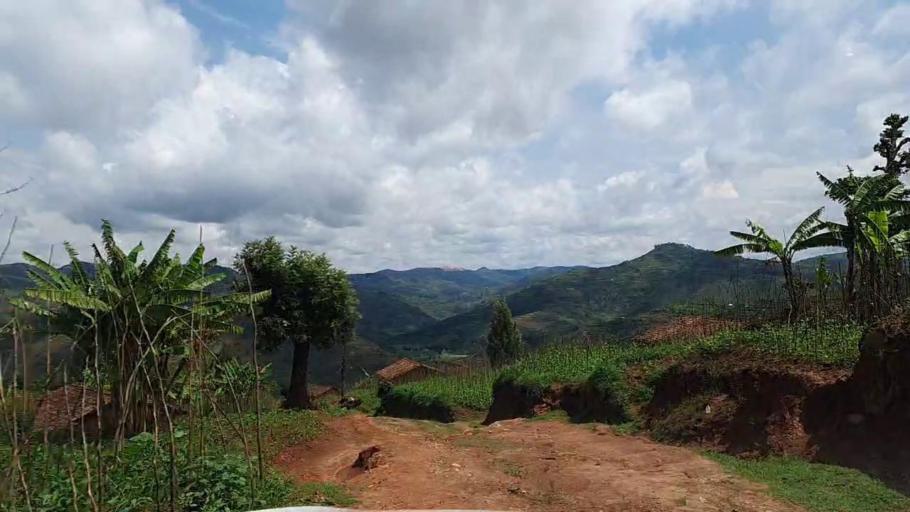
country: RW
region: Southern Province
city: Gikongoro
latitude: -2.3580
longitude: 29.5467
